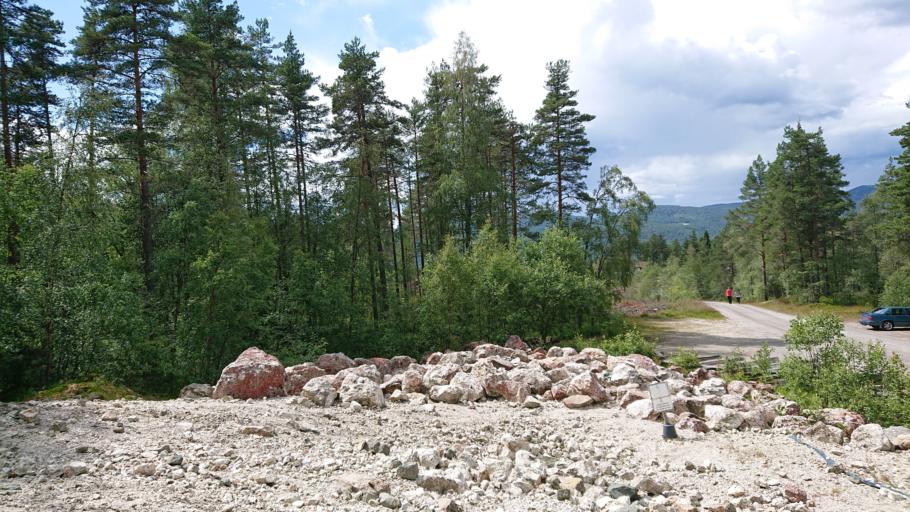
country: NO
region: Aust-Agder
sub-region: Evje og Hornnes
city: Evje
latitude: 58.5978
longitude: 7.8561
